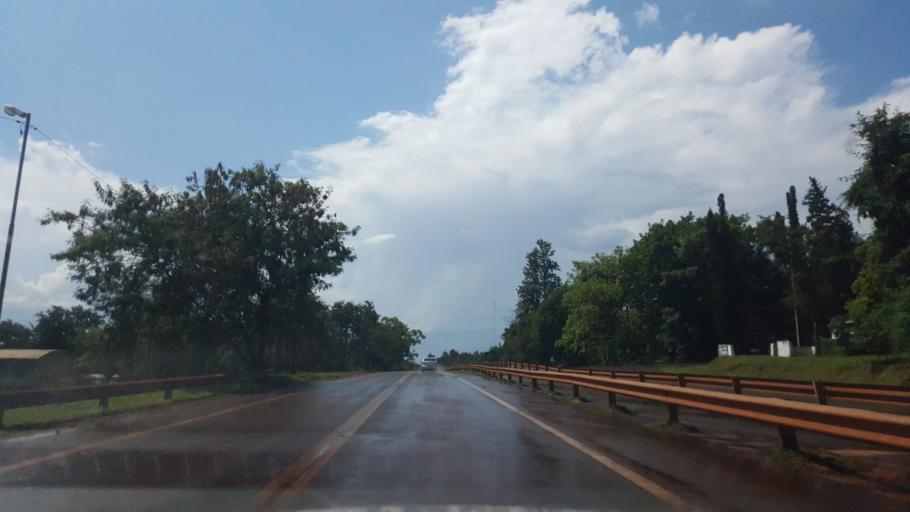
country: AR
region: Misiones
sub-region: Departamento de Eldorado
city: Eldorado
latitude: -26.3993
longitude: -54.6336
